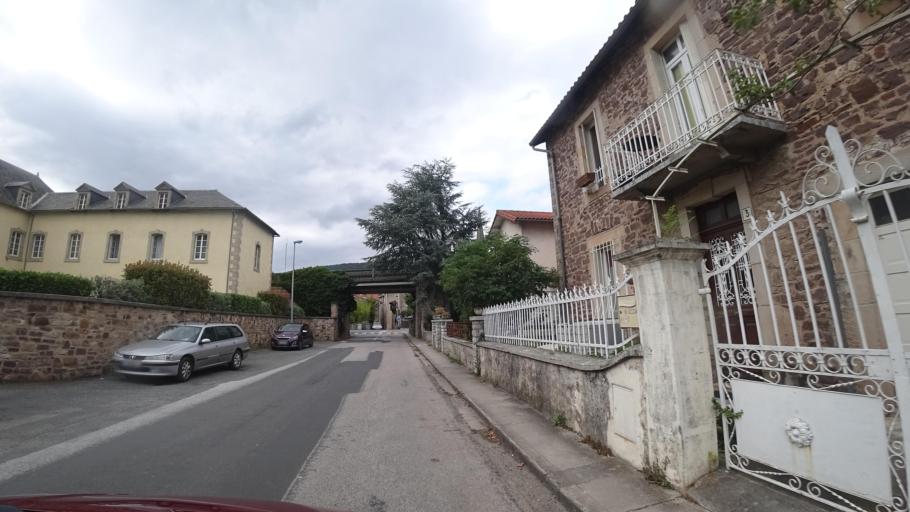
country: FR
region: Midi-Pyrenees
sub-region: Departement de l'Aveyron
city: Saint-Affrique
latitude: 43.9557
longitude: 2.8863
